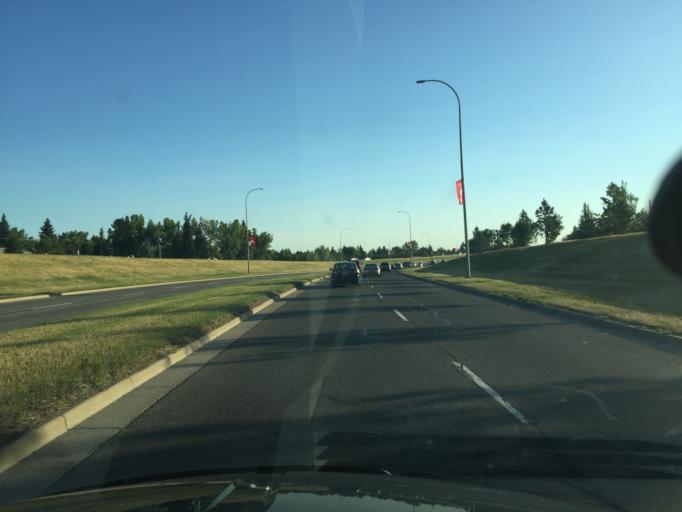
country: CA
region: Alberta
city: Calgary
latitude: 50.9355
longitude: -114.0330
